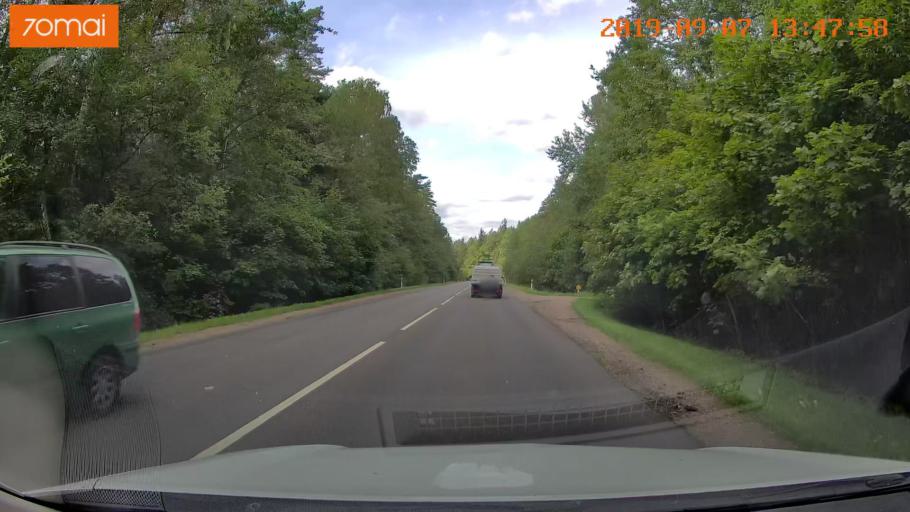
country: LT
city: Baltoji Voke
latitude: 54.6001
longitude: 25.2080
